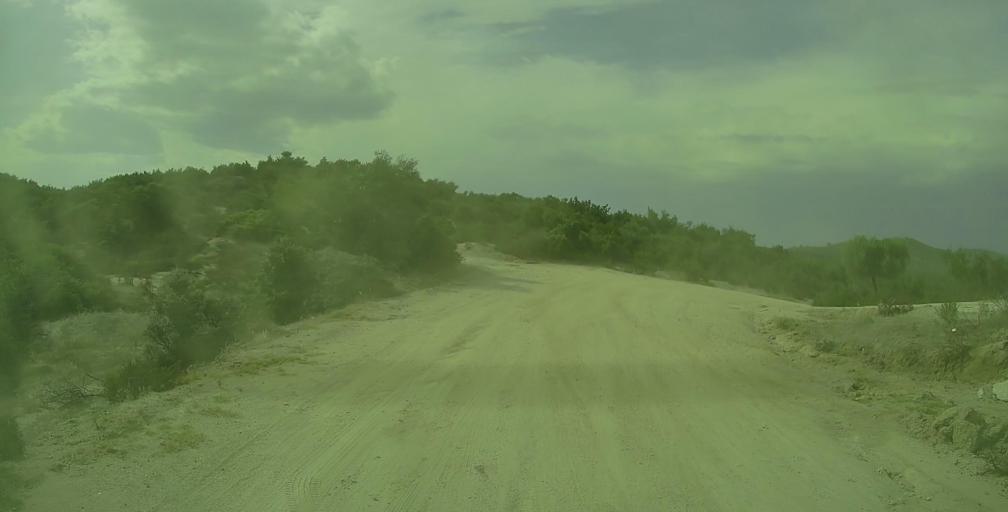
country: GR
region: Central Macedonia
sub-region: Nomos Chalkidikis
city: Sykia
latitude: 40.0023
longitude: 23.9244
